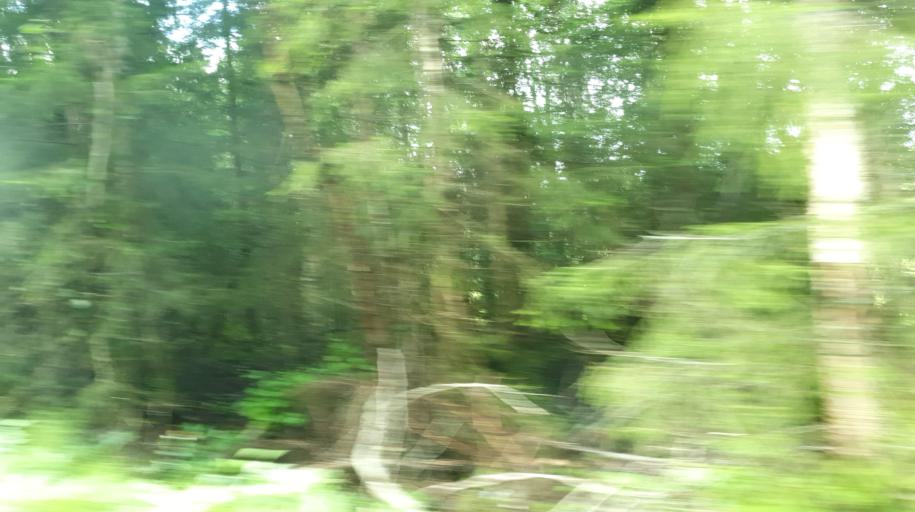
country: NO
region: Nord-Trondelag
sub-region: Levanger
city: Skogn
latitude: 63.5942
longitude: 11.2674
